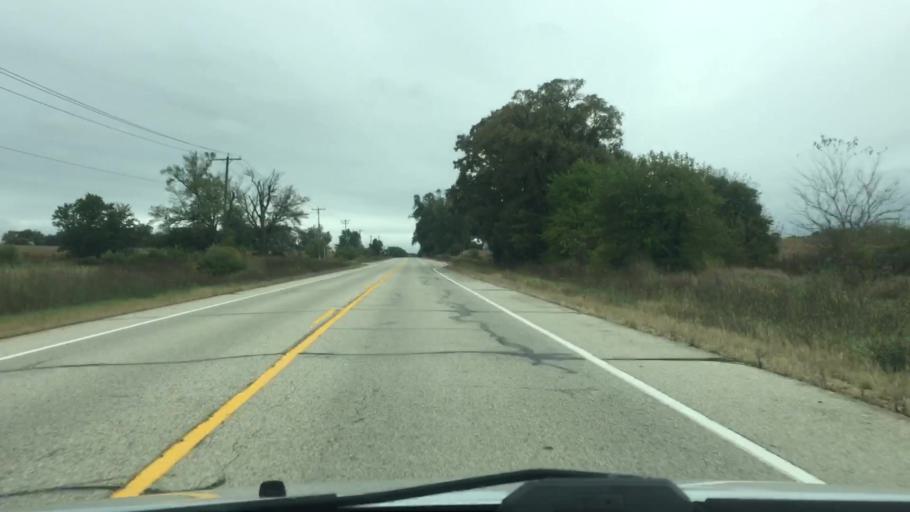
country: US
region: Wisconsin
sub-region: Jefferson County
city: Palmyra
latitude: 42.8304
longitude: -88.5485
